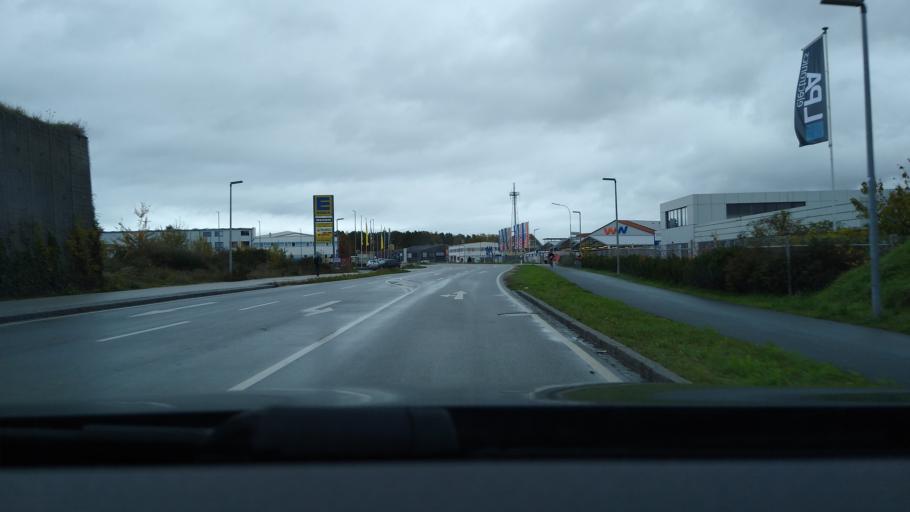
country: DE
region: Bavaria
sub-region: Regierungsbezirk Mittelfranken
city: Hemhofen
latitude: 49.6918
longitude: 10.9418
